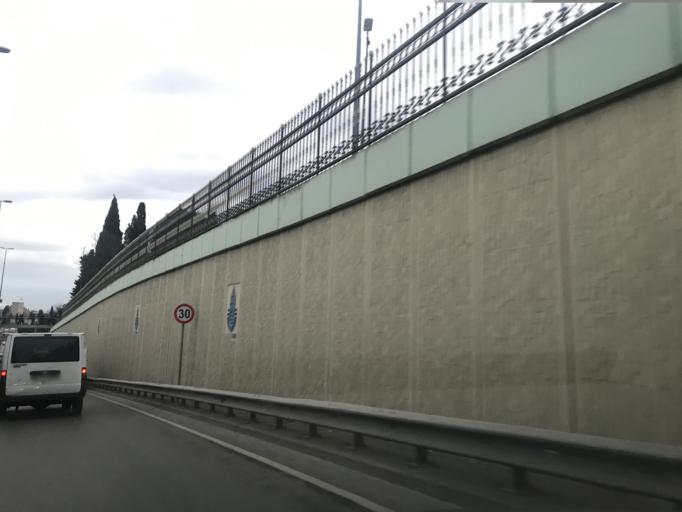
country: TR
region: Istanbul
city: Istanbul
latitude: 41.0342
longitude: 28.9277
